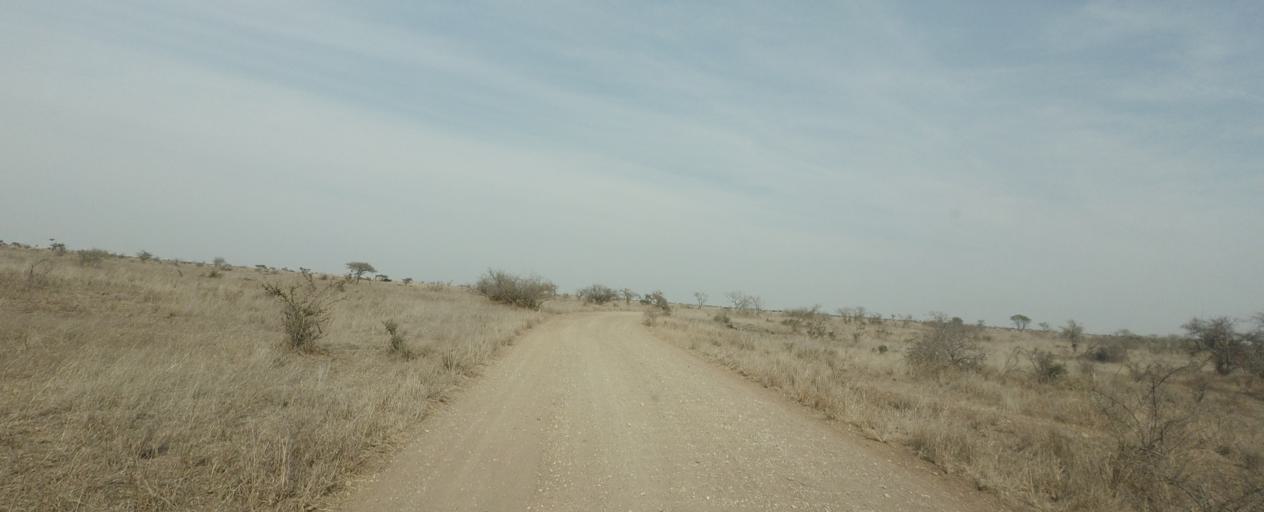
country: ZA
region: Limpopo
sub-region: Mopani District Municipality
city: Phalaborwa
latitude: -24.2604
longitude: 31.7216
